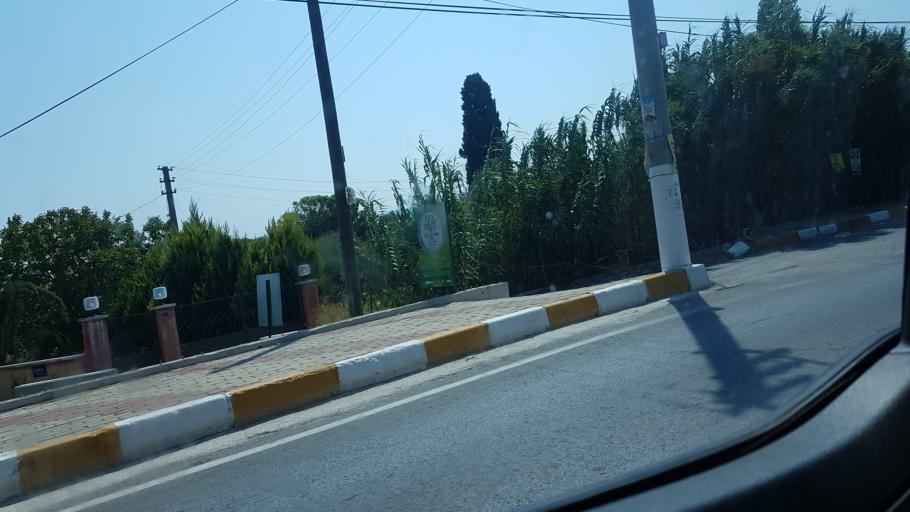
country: TR
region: Izmir
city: Urla
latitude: 38.3420
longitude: 26.7705
